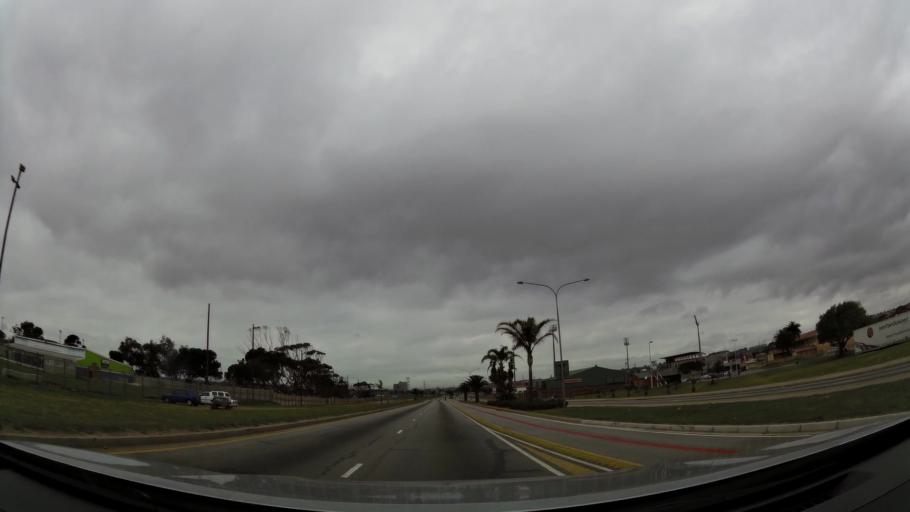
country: ZA
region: Eastern Cape
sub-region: Nelson Mandela Bay Metropolitan Municipality
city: Port Elizabeth
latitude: -33.9112
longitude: 25.5590
